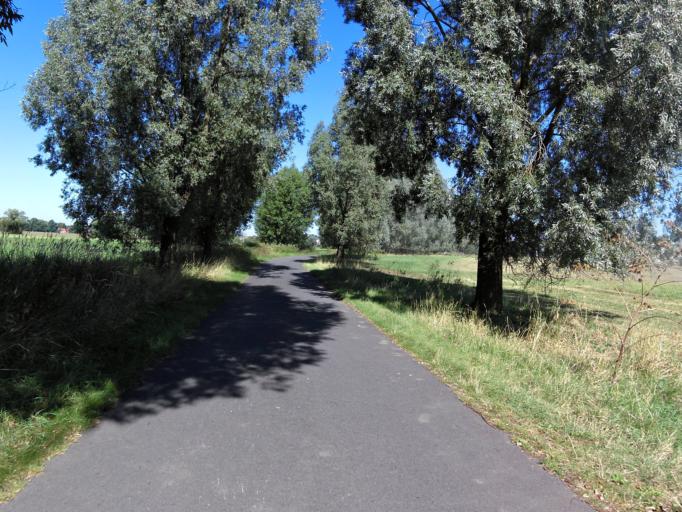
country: DE
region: Saxony-Anhalt
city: Pretzsch
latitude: 51.7086
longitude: 12.8168
